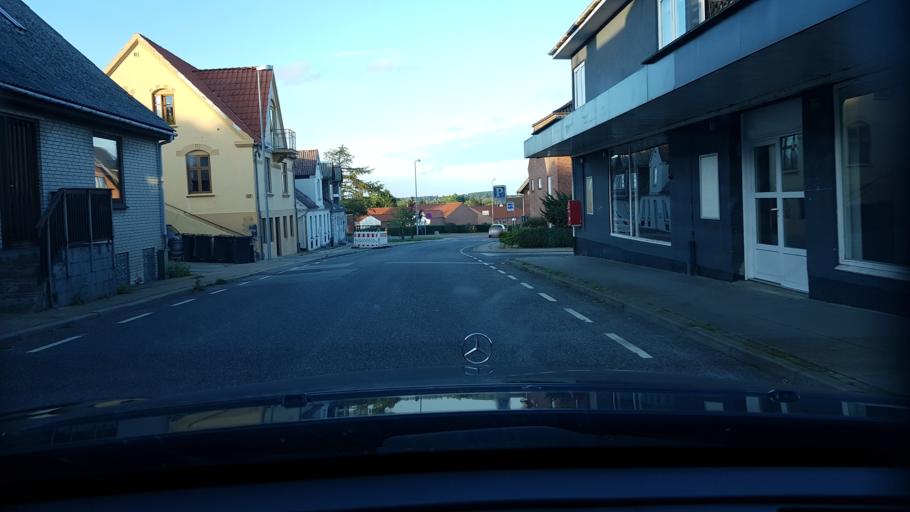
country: DK
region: North Denmark
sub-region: Mariagerfjord Kommune
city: Hadsund
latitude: 56.7208
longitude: 10.1183
